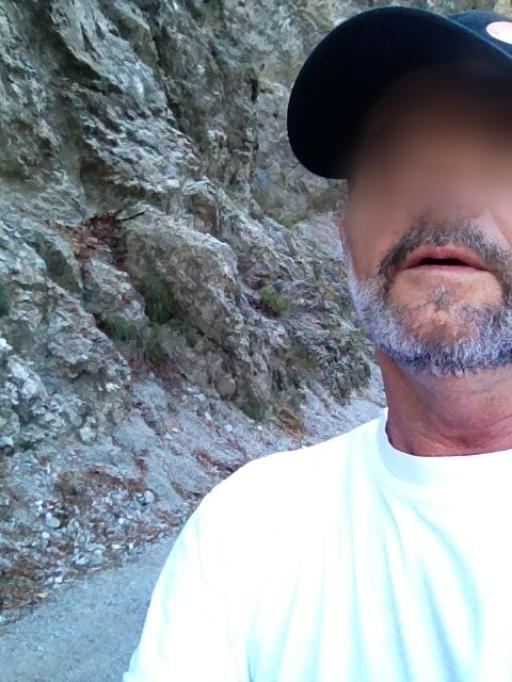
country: AL
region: Shkoder
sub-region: Rrethi i Shkodres
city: Nicaj-Shale
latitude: 42.3977
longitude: 19.7658
